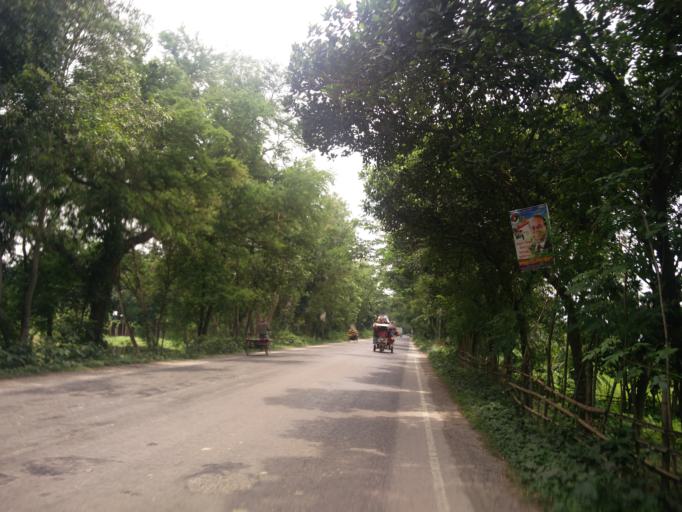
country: BD
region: Khulna
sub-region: Magura
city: Magura
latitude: 23.5460
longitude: 89.5247
